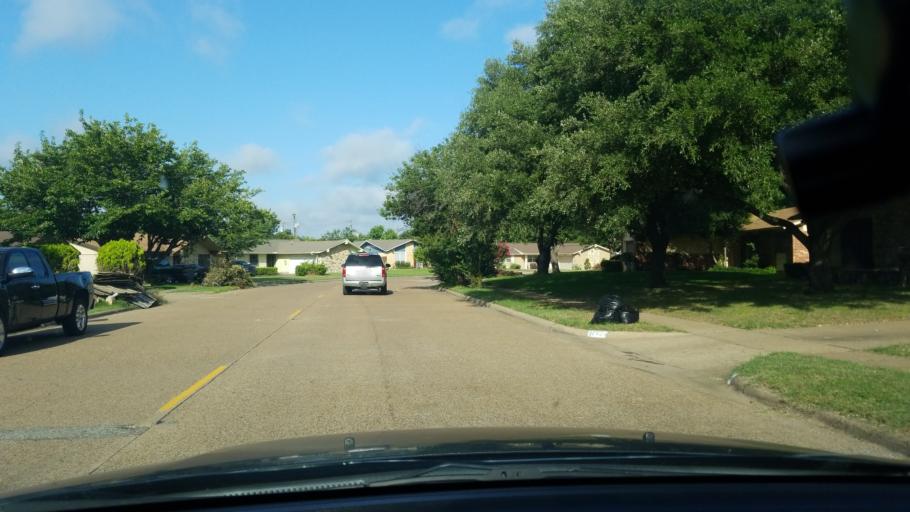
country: US
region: Texas
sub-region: Dallas County
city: Mesquite
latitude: 32.8150
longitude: -96.6854
